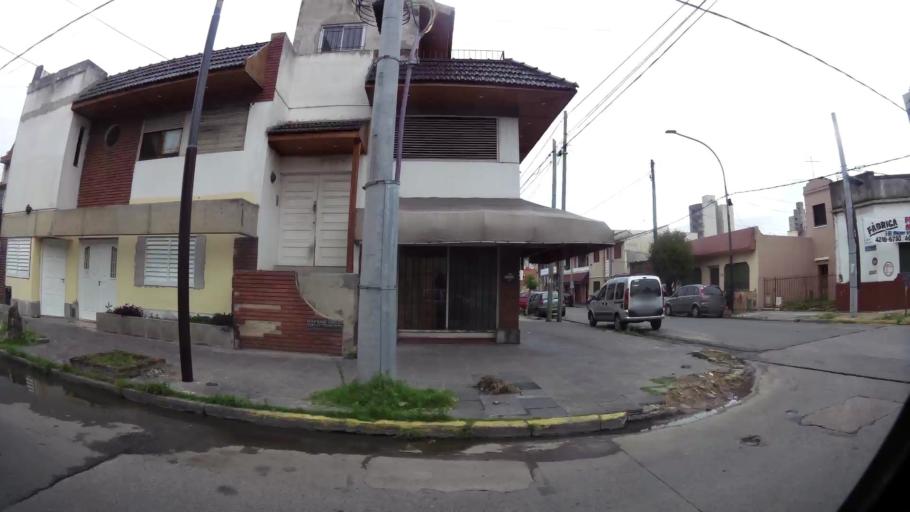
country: AR
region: Buenos Aires
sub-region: Partido de Lanus
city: Lanus
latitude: -34.7068
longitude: -58.3842
